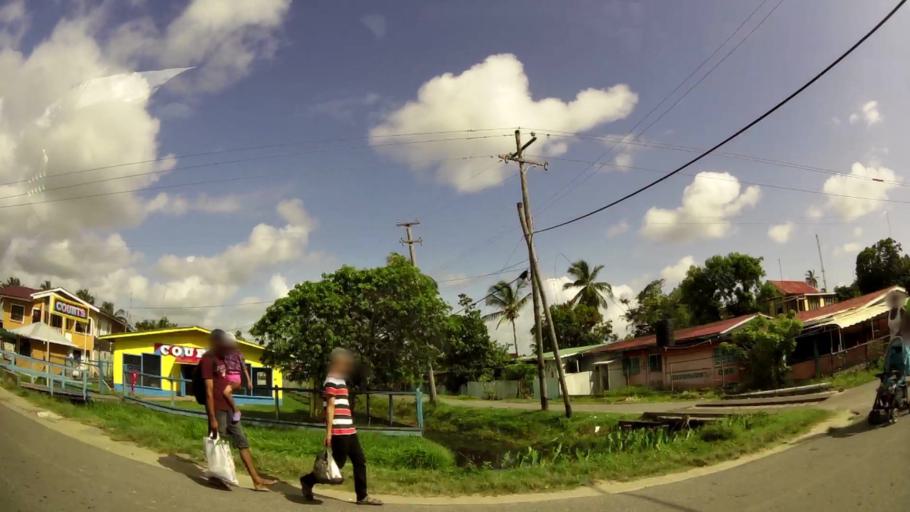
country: GY
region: Demerara-Mahaica
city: Mahaica Village
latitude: 6.6725
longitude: -57.9221
